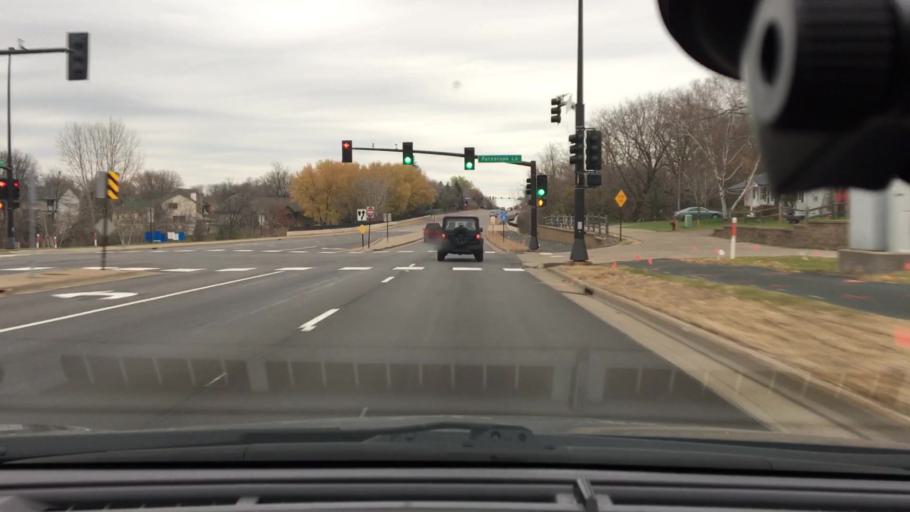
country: US
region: Minnesota
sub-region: Hennepin County
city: Maple Grove
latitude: 45.1235
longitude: -93.4622
